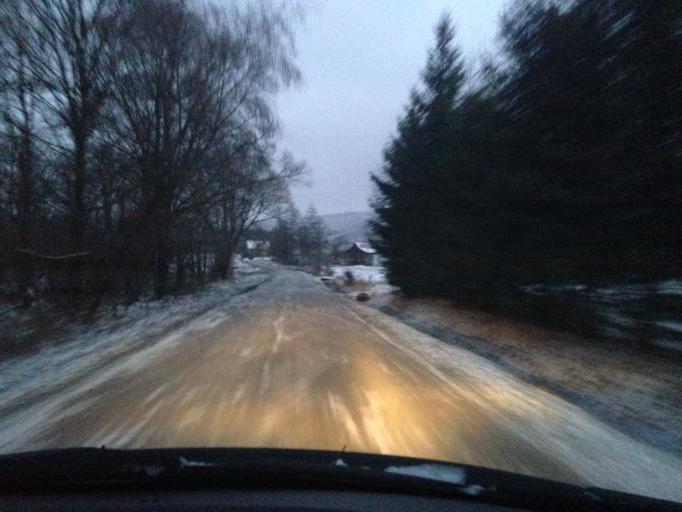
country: PL
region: Subcarpathian Voivodeship
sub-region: Powiat jasielski
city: Krempna
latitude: 49.5335
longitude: 21.5511
